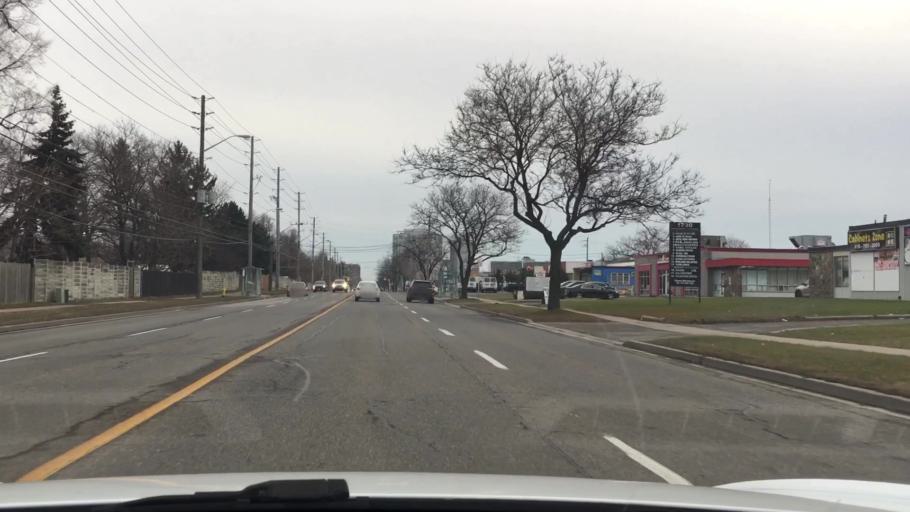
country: CA
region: Ontario
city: Scarborough
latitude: 43.7609
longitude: -79.2686
